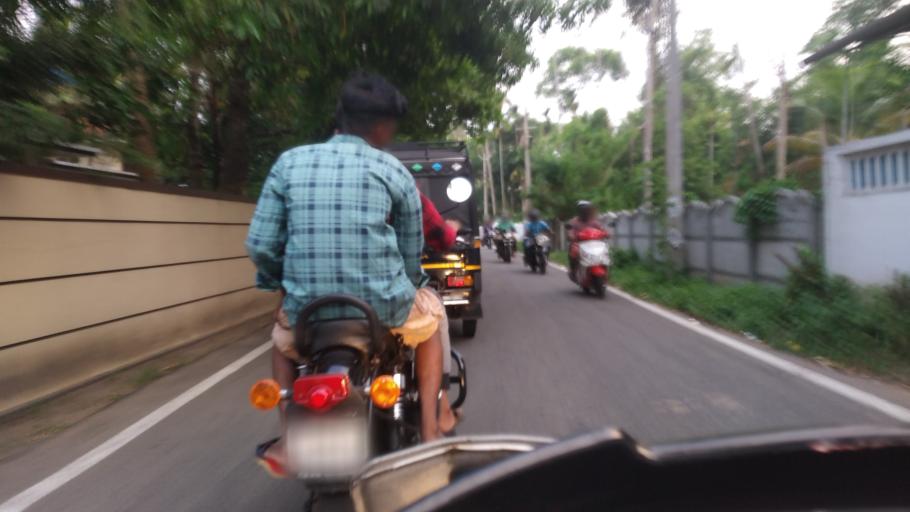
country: IN
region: Kerala
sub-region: Thrissur District
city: Kodungallur
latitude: 10.1621
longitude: 76.2098
